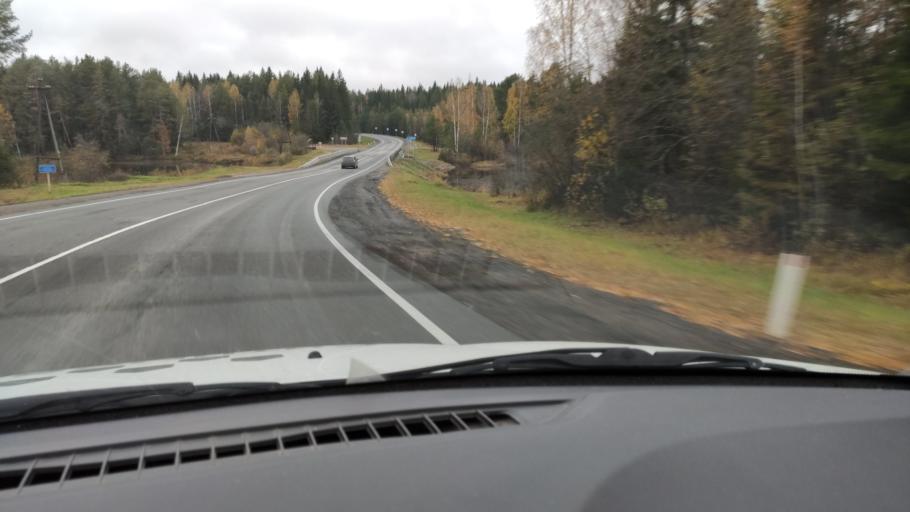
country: RU
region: Kirov
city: Belaya Kholunitsa
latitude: 58.9046
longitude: 50.9473
